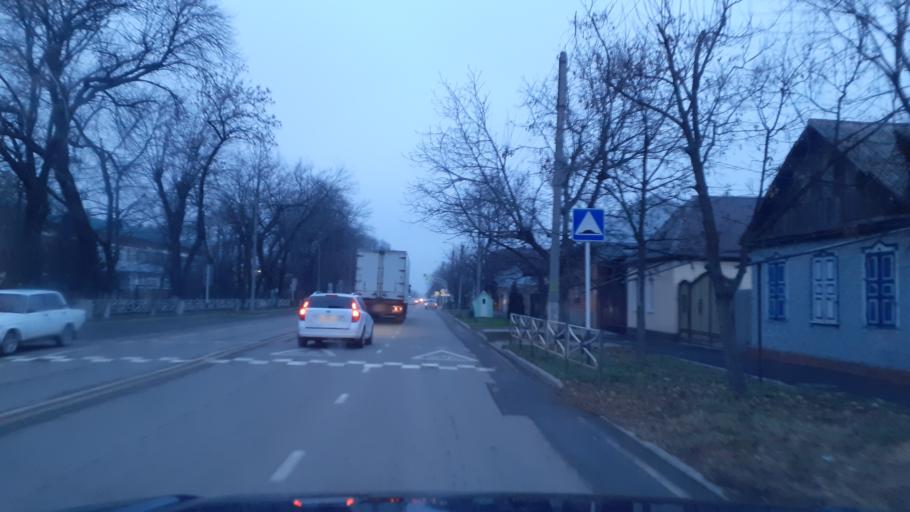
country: RU
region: Adygeya
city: Maykop
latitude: 44.6139
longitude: 40.0939
